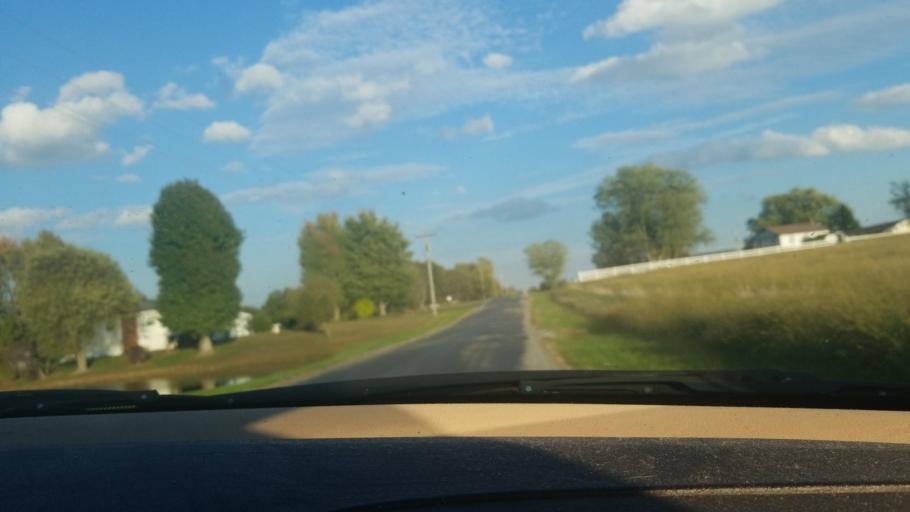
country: US
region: Illinois
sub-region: Saline County
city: Carrier Mills
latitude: 37.7718
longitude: -88.7426
